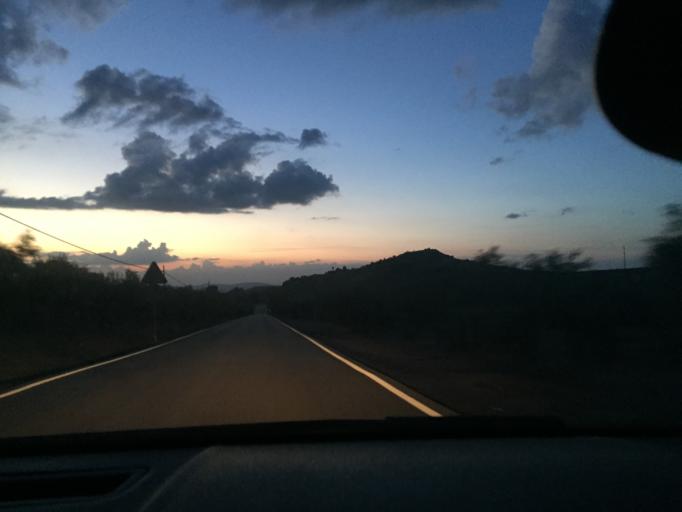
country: ES
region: Andalusia
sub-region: Provincia de Jaen
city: Mancha Real
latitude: 37.7989
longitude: -3.6542
